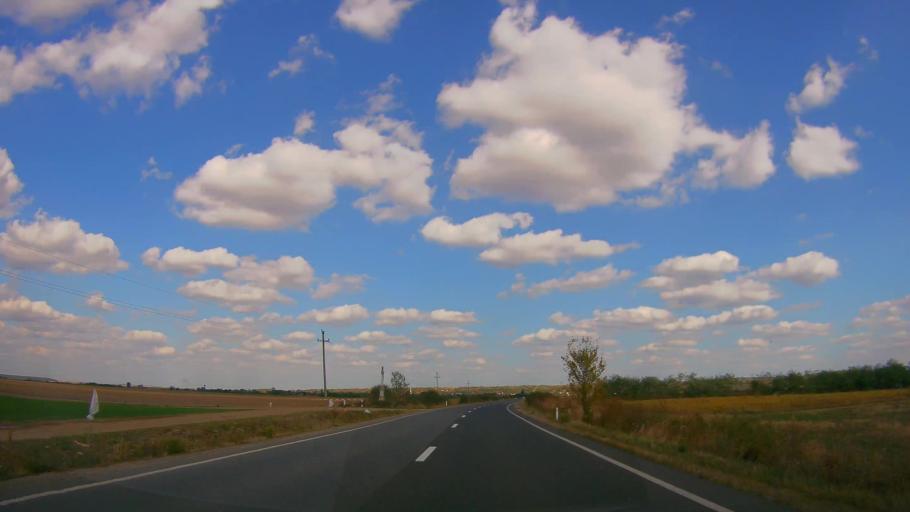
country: RO
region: Satu Mare
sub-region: Comuna Beltiug
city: Beltiug
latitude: 47.5406
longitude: 22.8170
